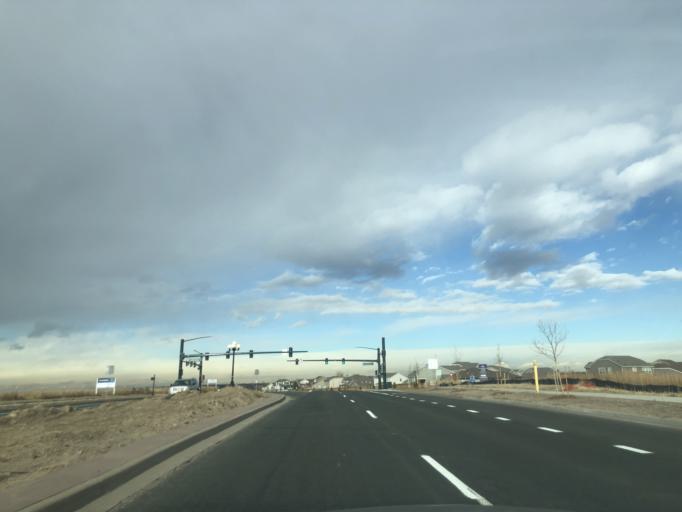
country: US
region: Colorado
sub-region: Douglas County
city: Stonegate
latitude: 39.5552
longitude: -104.8073
